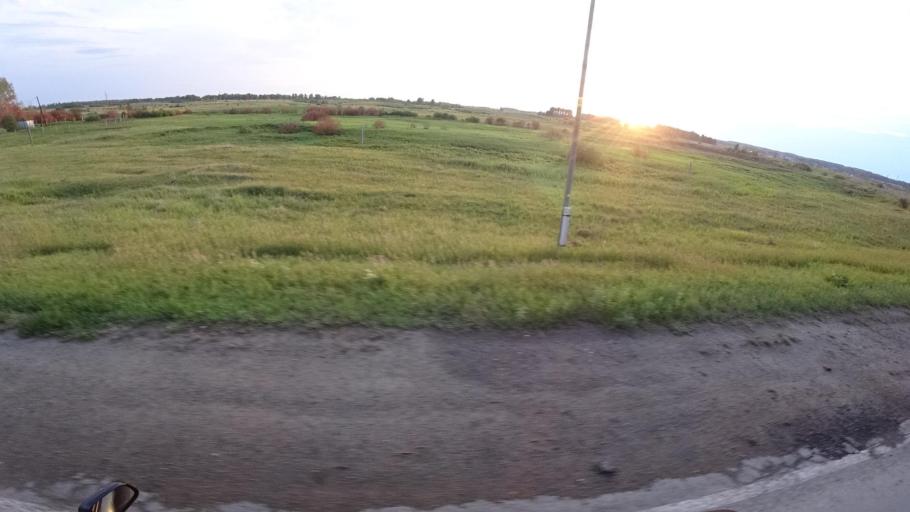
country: RU
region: Sverdlovsk
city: Kamyshlov
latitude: 56.8689
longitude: 62.7109
